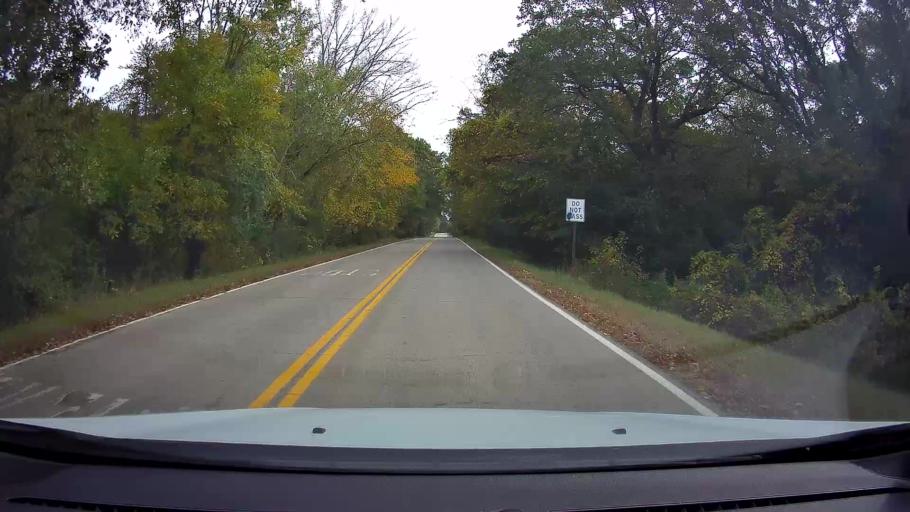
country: US
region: Minnesota
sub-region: Washington County
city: Stillwater
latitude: 45.1066
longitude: -92.7936
